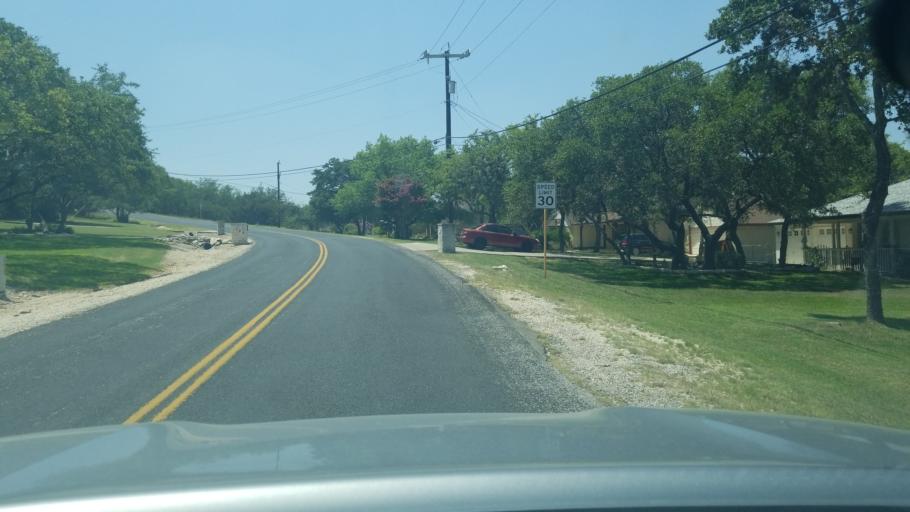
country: US
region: Texas
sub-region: Bexar County
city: Timberwood Park
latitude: 29.6827
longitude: -98.4960
